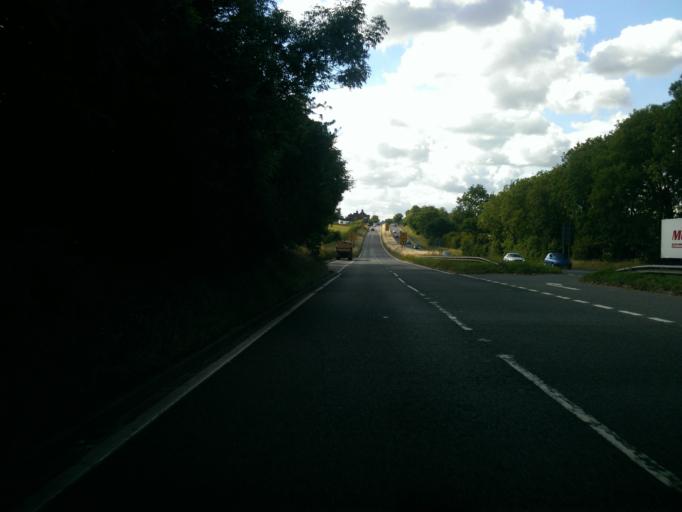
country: GB
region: England
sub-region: Warwickshire
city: Atherstone
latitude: 52.5850
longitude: -1.5731
